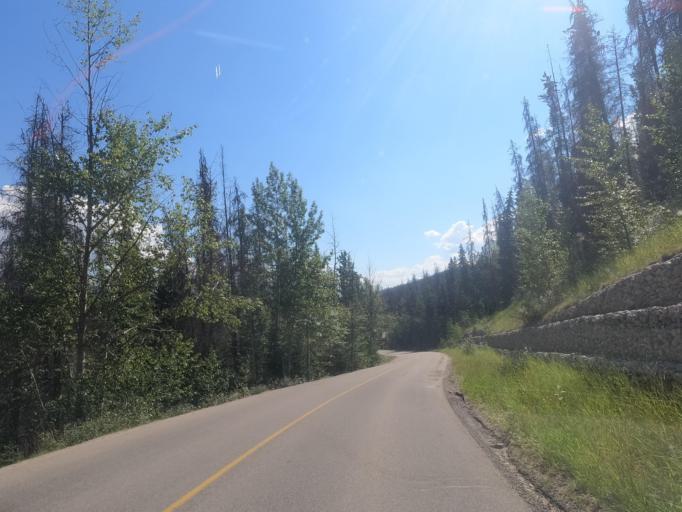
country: CA
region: Alberta
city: Jasper Park Lodge
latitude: 52.8574
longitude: -118.0960
